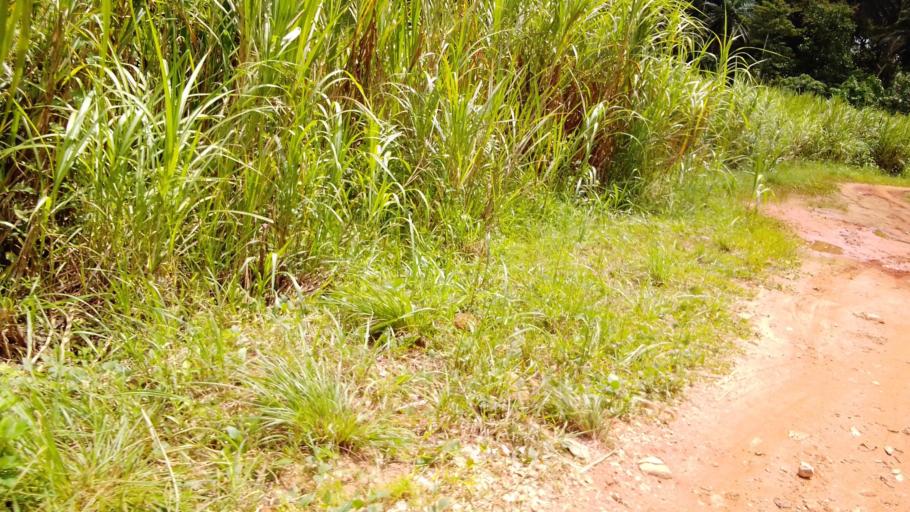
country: SL
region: Eastern Province
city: Koyima
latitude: 8.6806
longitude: -11.0053
